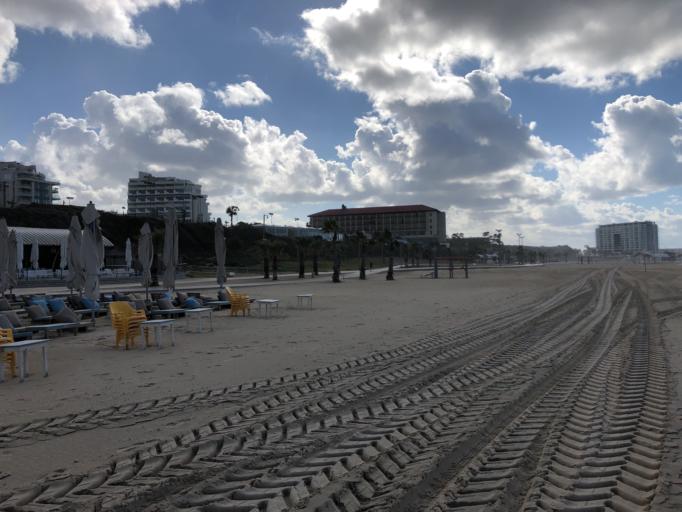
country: IL
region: Tel Aviv
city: Herzliya Pituah
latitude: 32.1701
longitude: 34.7990
